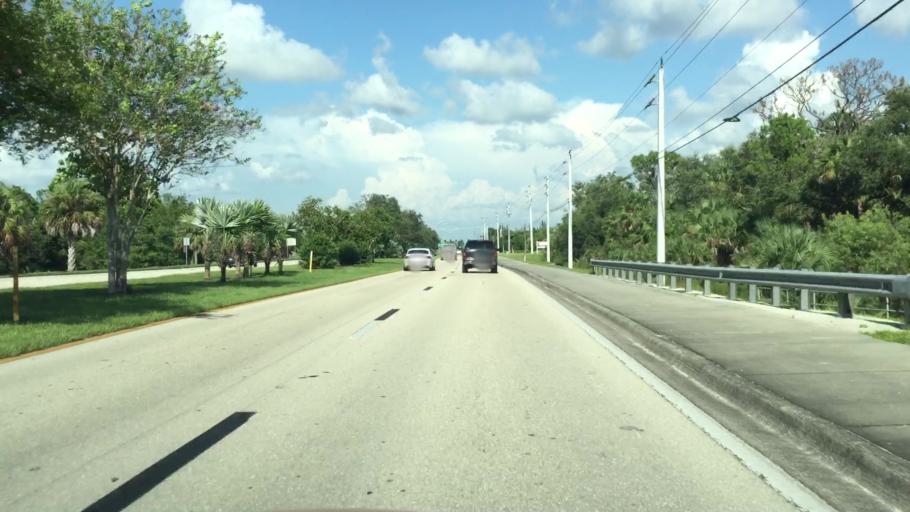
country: US
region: Florida
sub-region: Lee County
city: Estero
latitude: 26.4312
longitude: -81.7935
